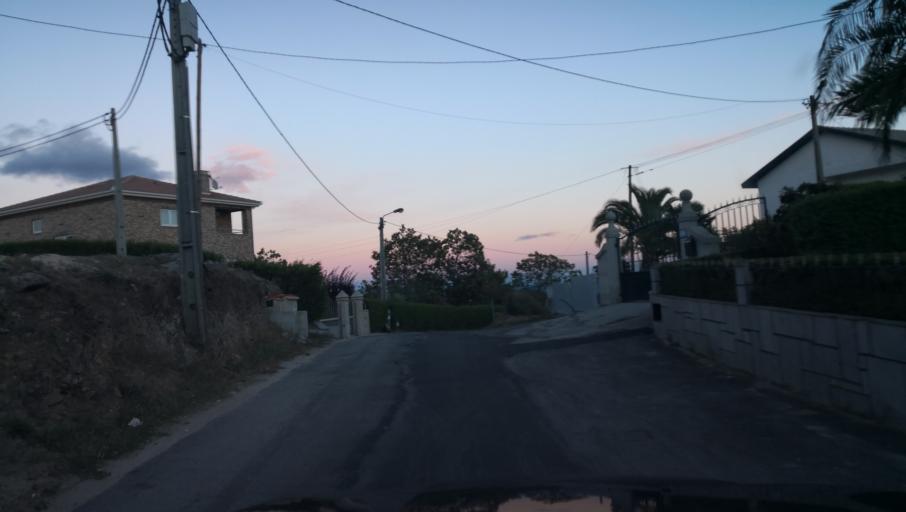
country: PT
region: Vila Real
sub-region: Santa Marta de Penaguiao
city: Santa Marta de Penaguiao
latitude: 41.2682
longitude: -7.8072
